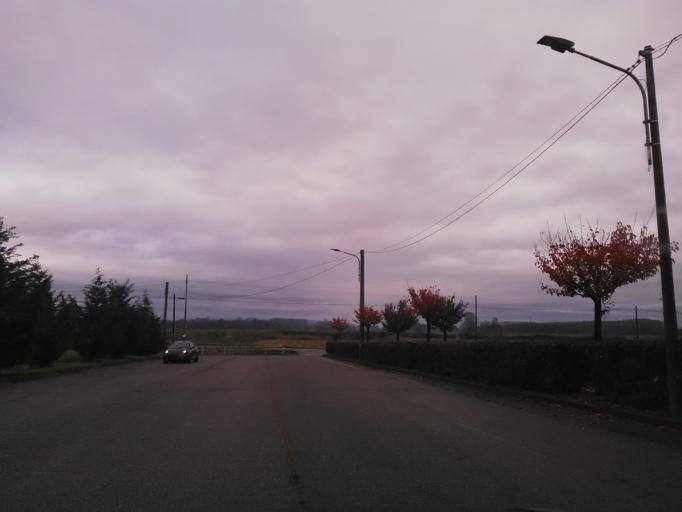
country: IT
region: Piedmont
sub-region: Provincia di Vercelli
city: Carisio
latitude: 45.4058
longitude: 8.2035
